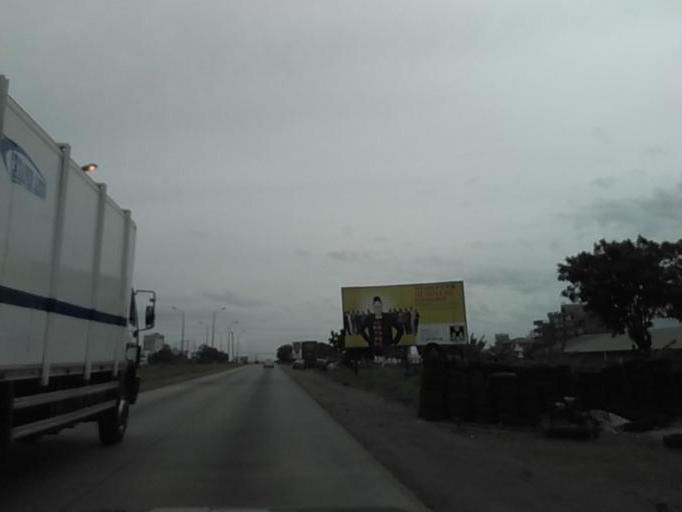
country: GH
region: Greater Accra
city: Medina Estates
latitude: 5.6262
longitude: -0.1671
